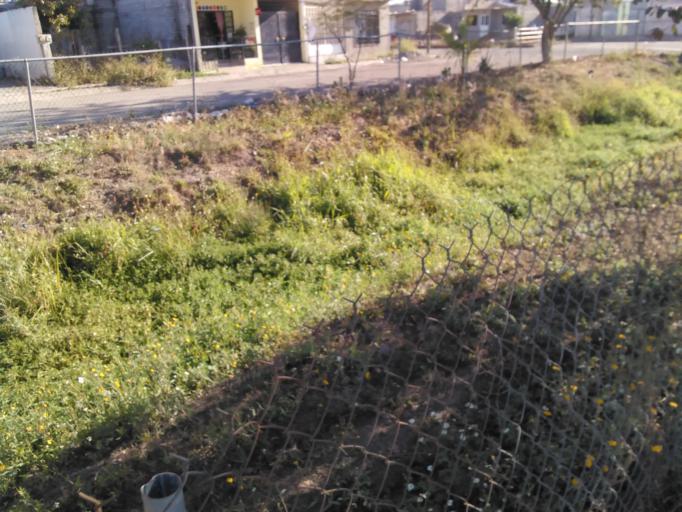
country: MX
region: Nayarit
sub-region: Tepic
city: La Corregidora
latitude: 21.4851
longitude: -104.8344
